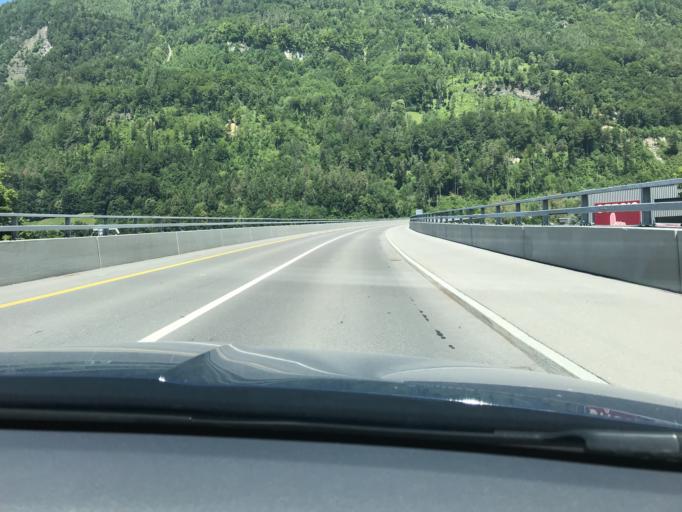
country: CH
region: Bern
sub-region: Interlaken-Oberhasli District
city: Interlaken
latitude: 46.6899
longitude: 7.8738
